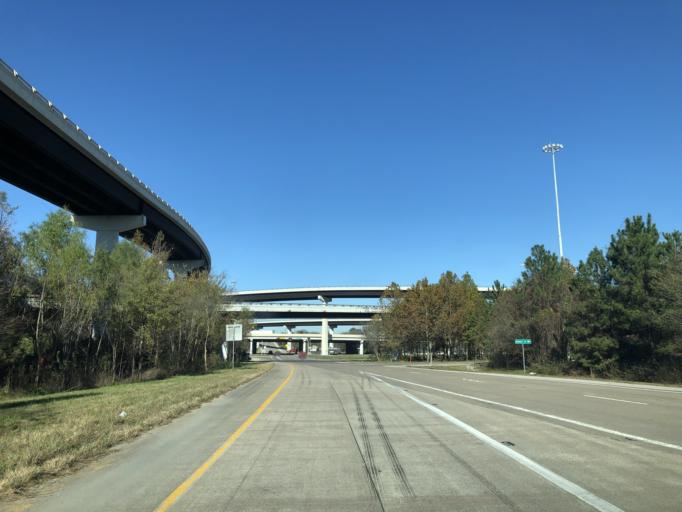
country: US
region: Texas
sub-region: Harris County
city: Cloverleaf
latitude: 29.7694
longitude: -95.1510
